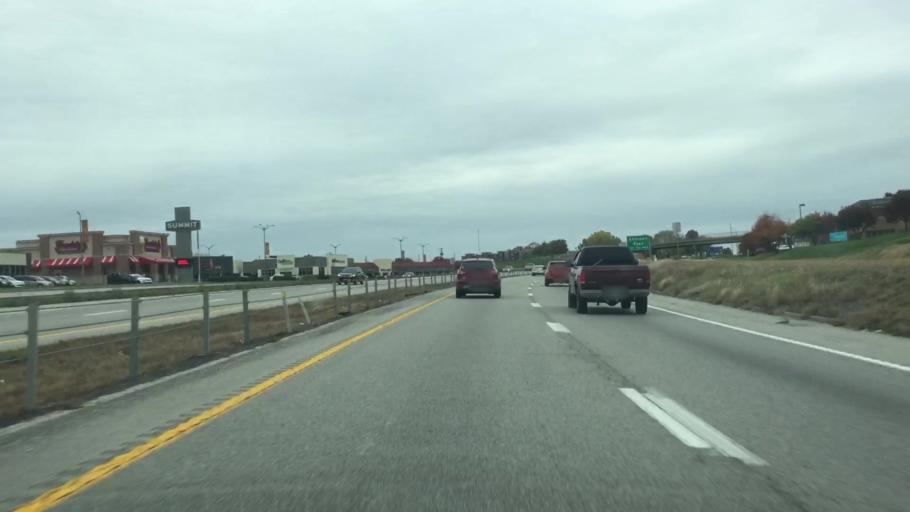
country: US
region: Missouri
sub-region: Jackson County
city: Lees Summit
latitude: 38.9162
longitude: -94.3996
